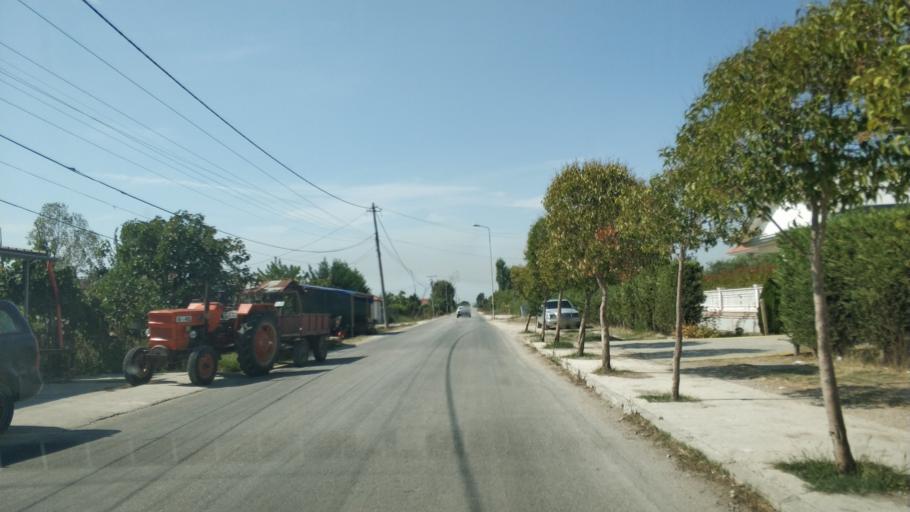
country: AL
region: Fier
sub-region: Rrethi i Fierit
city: Dermenas
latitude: 40.7460
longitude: 19.4912
